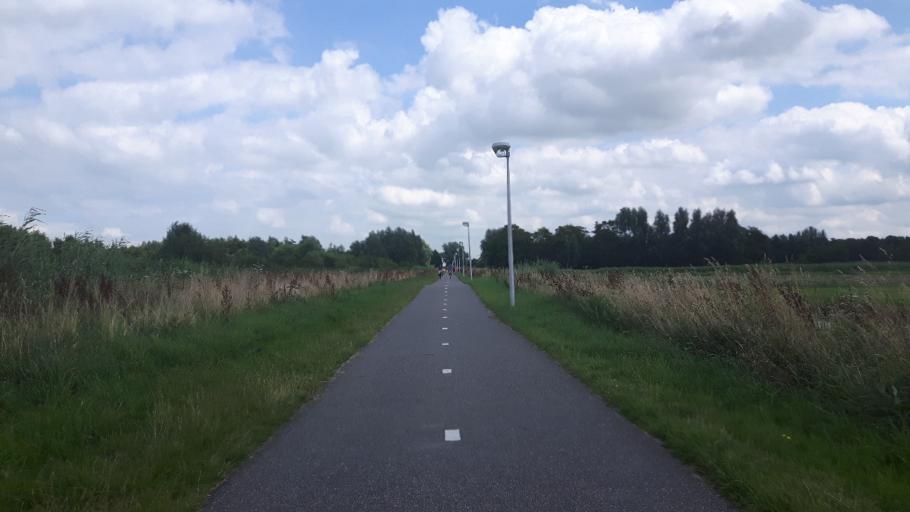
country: NL
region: South Holland
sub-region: Gemeente Krimpen aan den IJssel
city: Krimpen aan den IJssel
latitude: 51.9047
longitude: 4.6251
